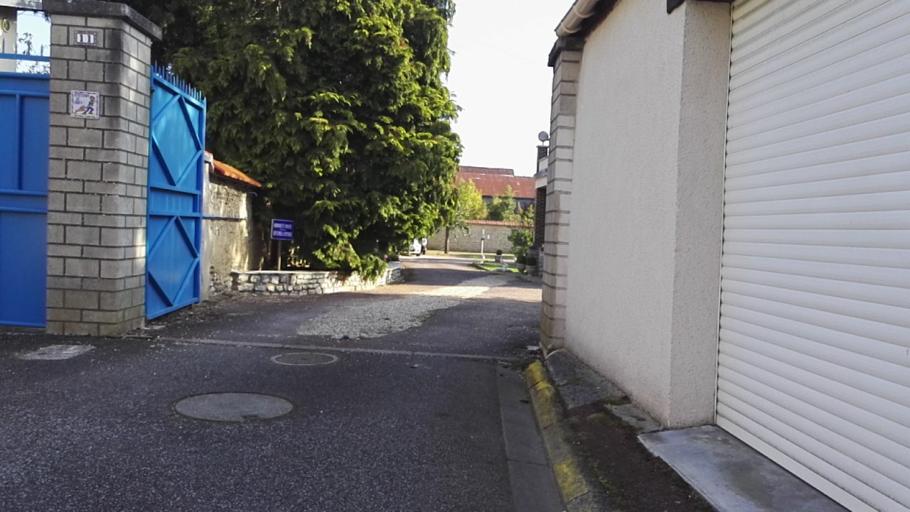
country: FR
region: Haute-Normandie
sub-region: Departement de l'Eure
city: Pacy-sur-Eure
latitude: 49.0159
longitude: 1.3795
